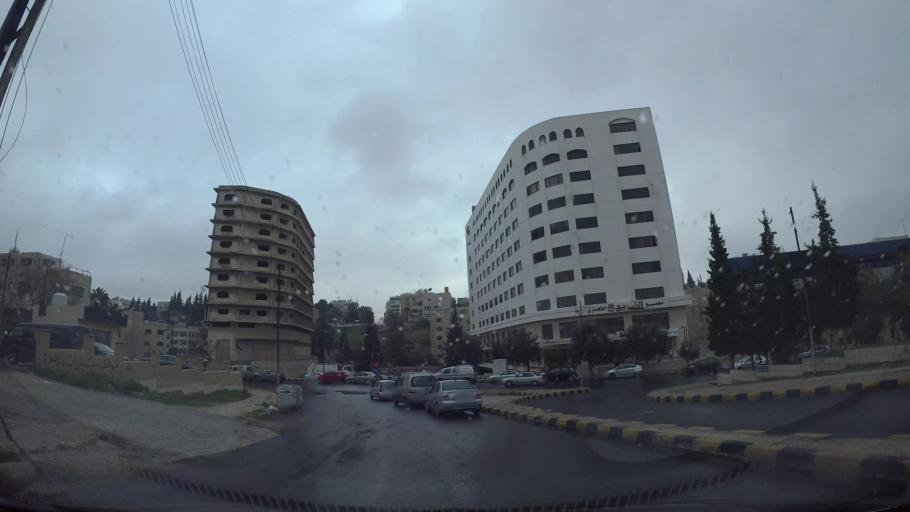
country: JO
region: Amman
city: Amman
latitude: 31.9634
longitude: 35.9142
